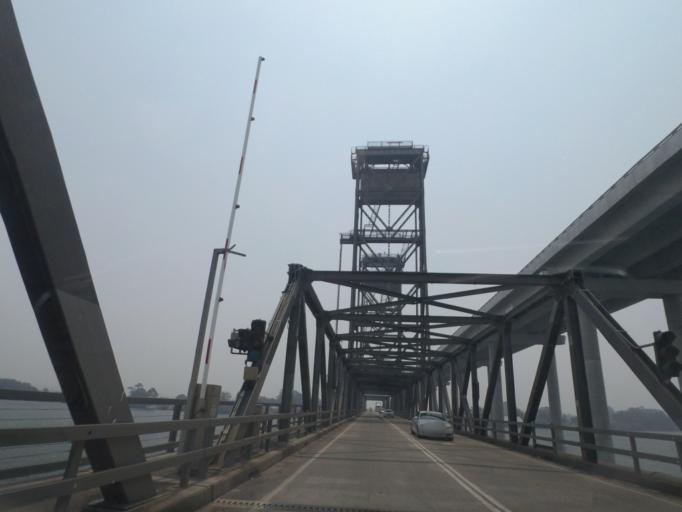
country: AU
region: New South Wales
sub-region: Clarence Valley
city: Maclean
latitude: -29.4307
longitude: 153.2408
